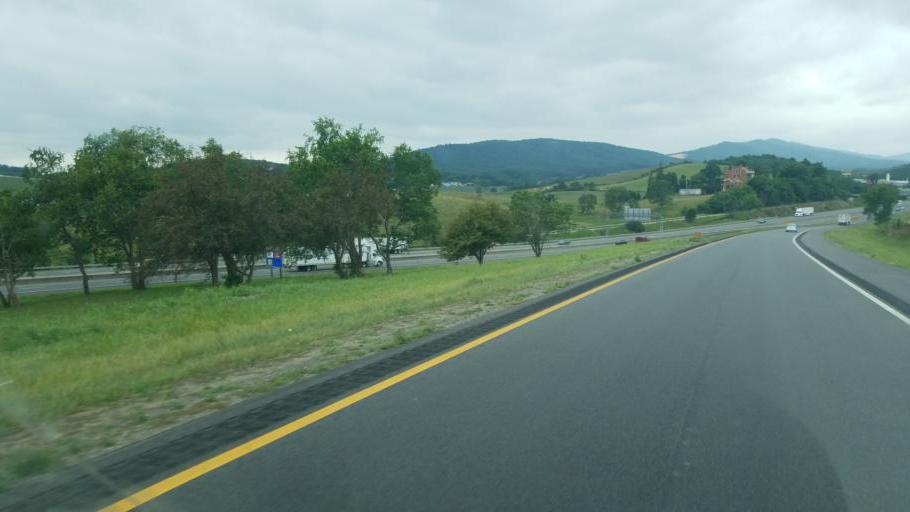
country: US
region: Virginia
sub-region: Wythe County
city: Wytheville
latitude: 36.9489
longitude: -80.9314
